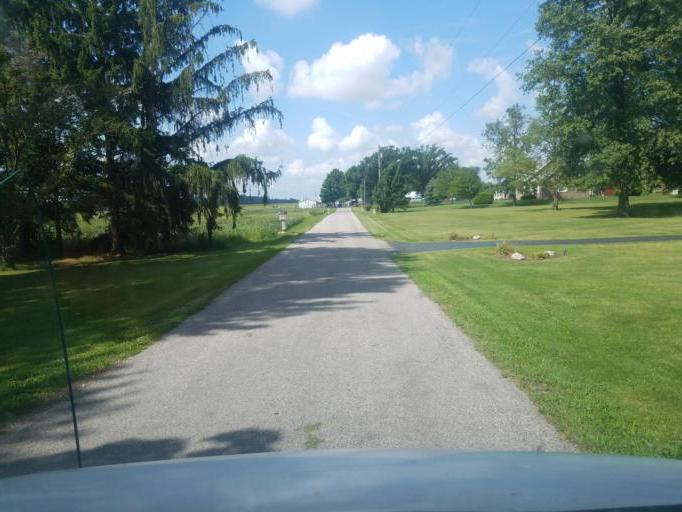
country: US
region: Ohio
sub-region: Marion County
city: Prospect
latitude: 40.4911
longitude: -83.1292
